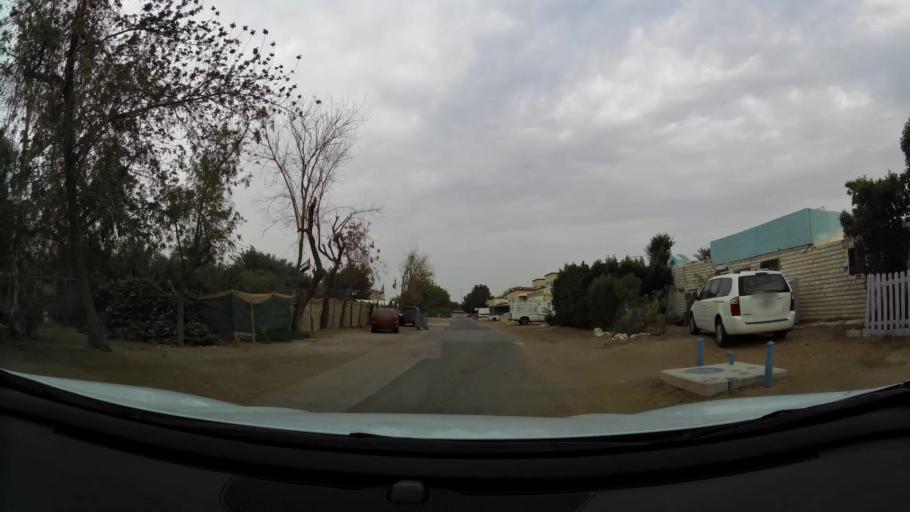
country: AE
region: Abu Dhabi
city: Al Ain
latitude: 24.2223
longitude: 55.7352
